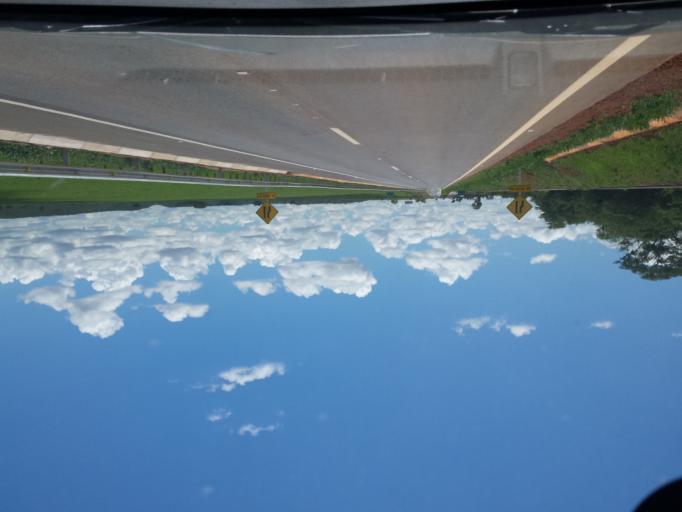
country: BR
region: Goias
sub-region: Cristalina
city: Cristalina
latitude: -16.6103
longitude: -47.7631
